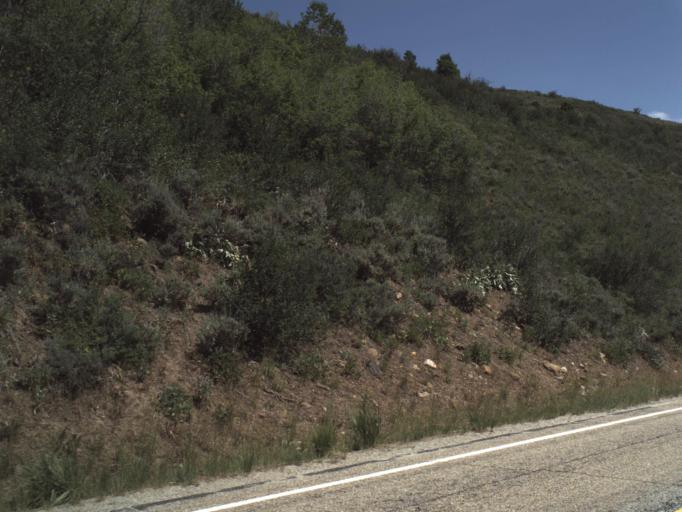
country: US
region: Utah
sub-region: Weber County
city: Wolf Creek
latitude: 41.3787
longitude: -111.5904
